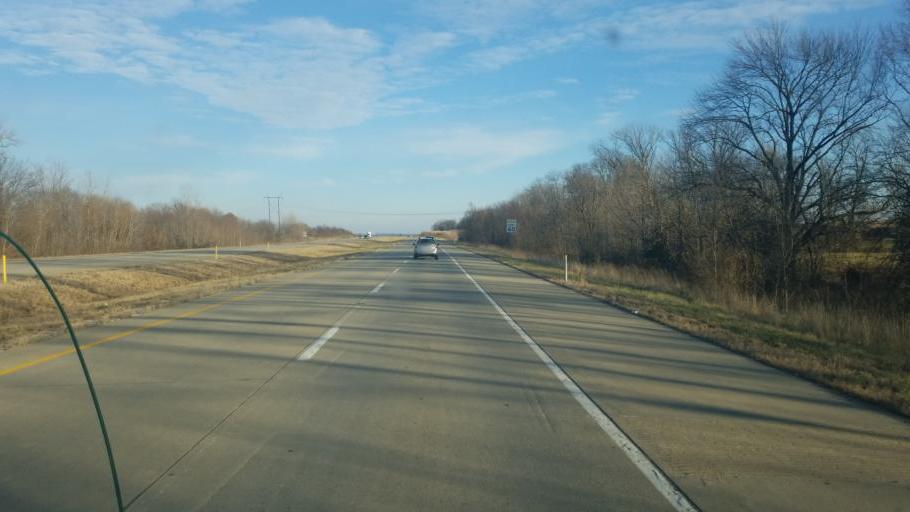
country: US
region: Indiana
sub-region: Knox County
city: Vincennes
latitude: 38.6789
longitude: -87.4013
